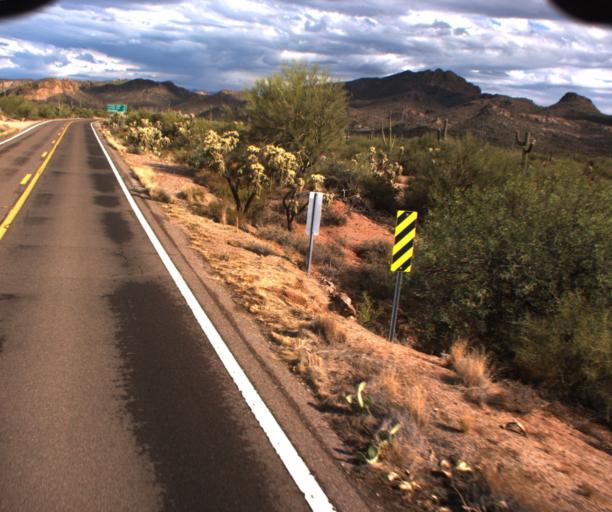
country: US
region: Arizona
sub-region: Pinal County
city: Apache Junction
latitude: 33.4908
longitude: -111.4673
